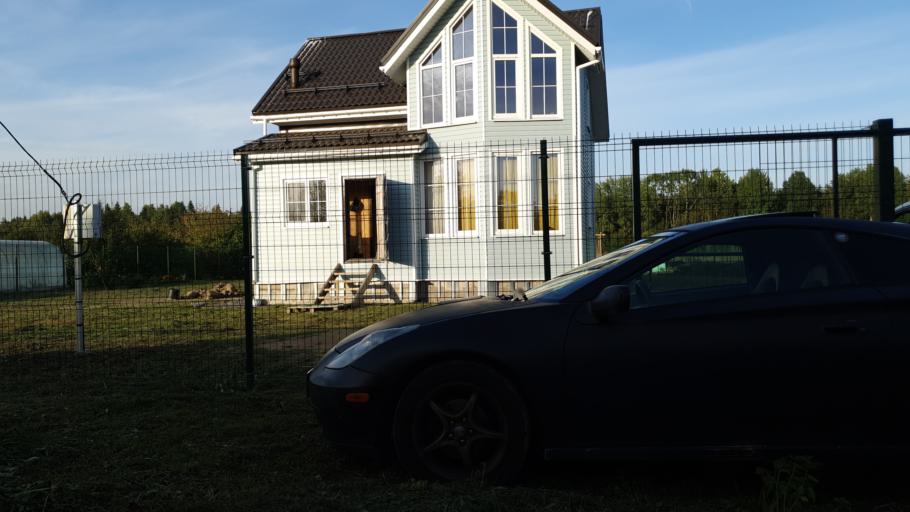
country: RU
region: Leningrad
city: Ivangorod
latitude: 59.4283
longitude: 28.3231
